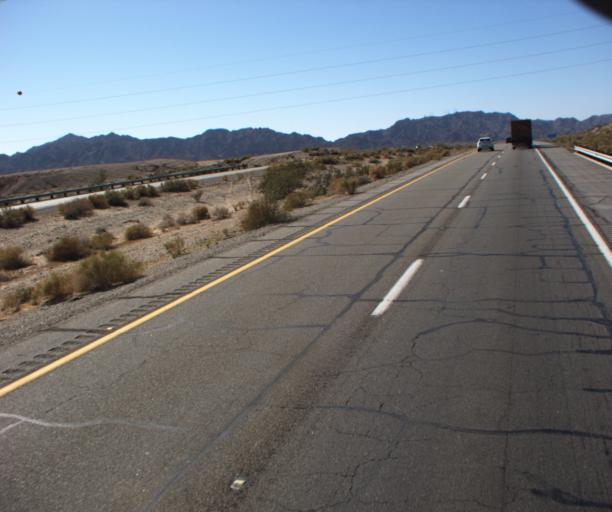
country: US
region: Arizona
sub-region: Yuma County
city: Wellton
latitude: 32.6613
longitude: -114.2595
